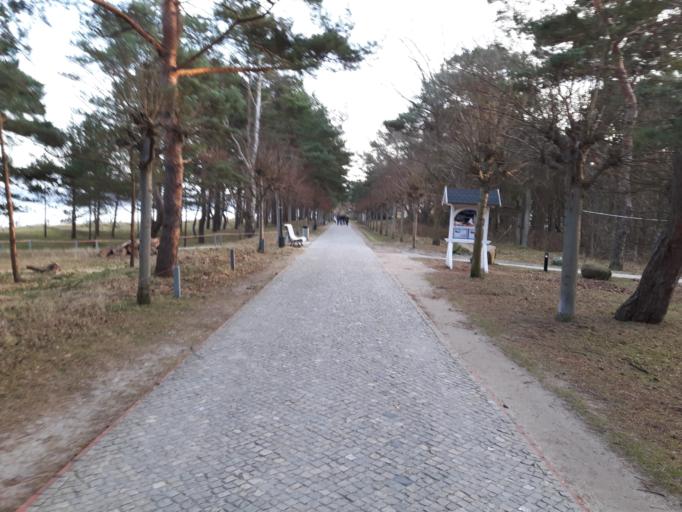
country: DE
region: Mecklenburg-Vorpommern
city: Ostseebad Binz
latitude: 54.4147
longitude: 13.5966
